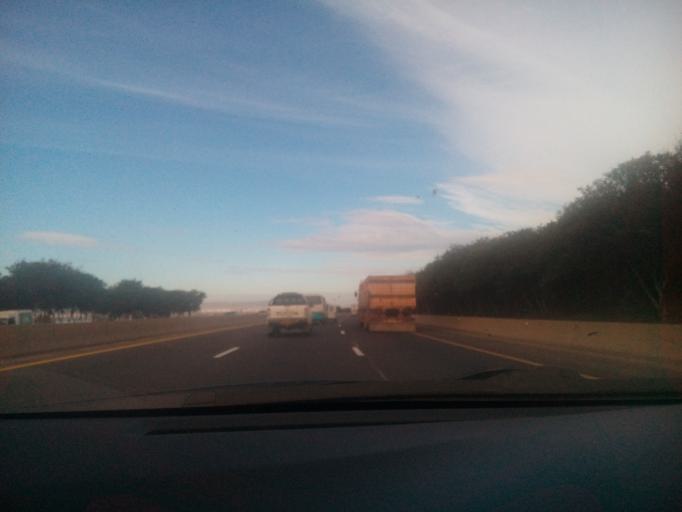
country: DZ
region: Oran
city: Es Senia
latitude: 35.5811
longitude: -0.5697
